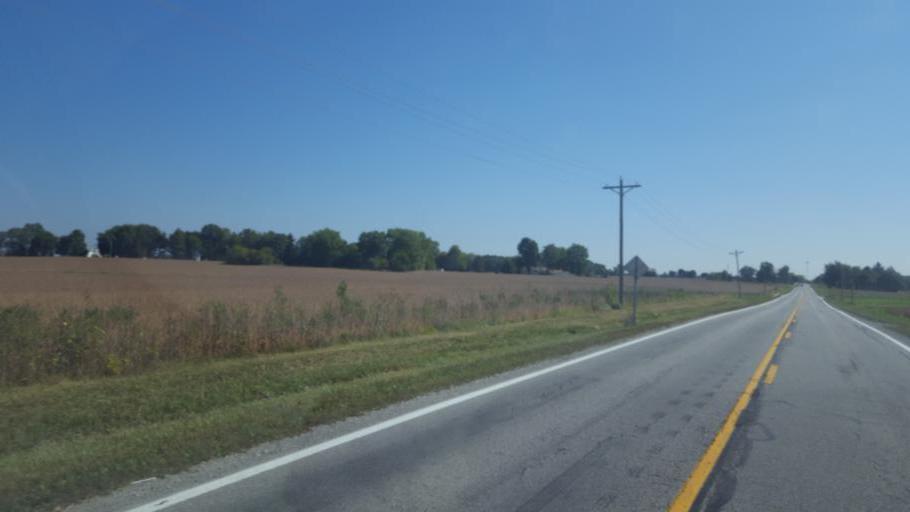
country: US
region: Ohio
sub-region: Marion County
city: Marion
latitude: 40.6227
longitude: -83.2503
